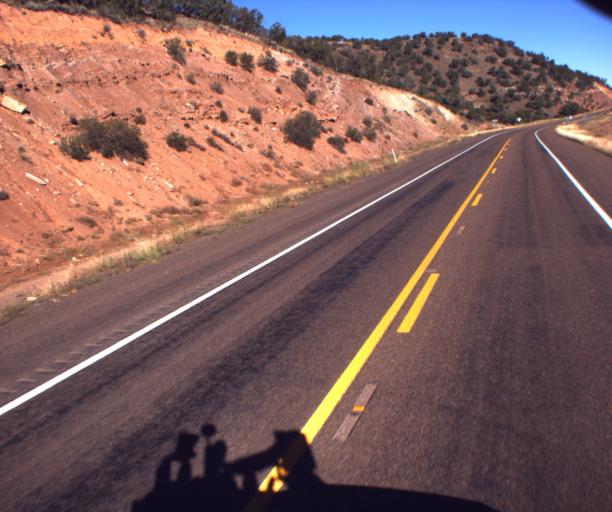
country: US
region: Arizona
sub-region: Navajo County
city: White Mountain Lake
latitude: 34.3885
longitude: -110.0631
